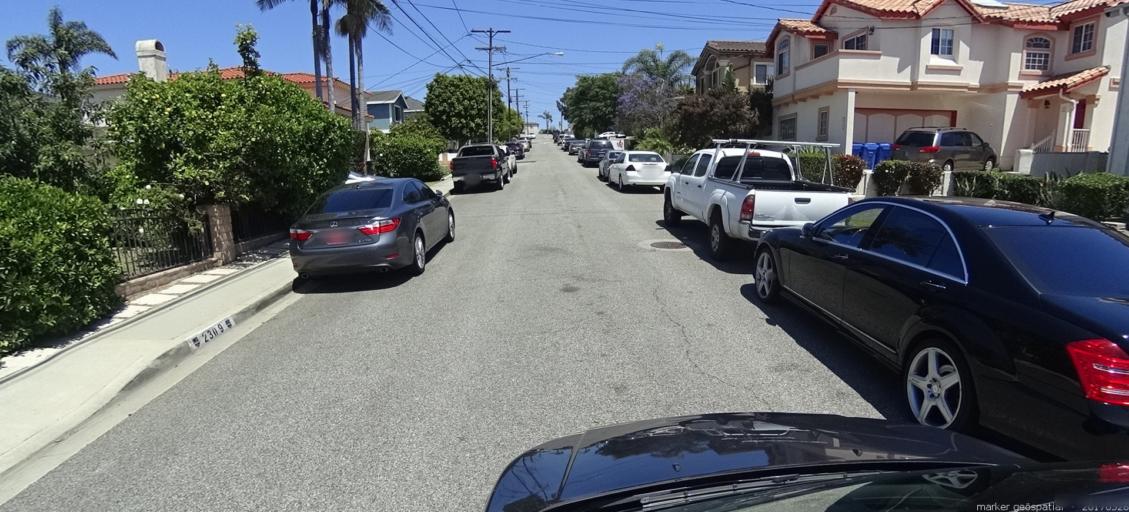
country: US
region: California
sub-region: Los Angeles County
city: Redondo Beach
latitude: 33.8643
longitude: -118.3699
